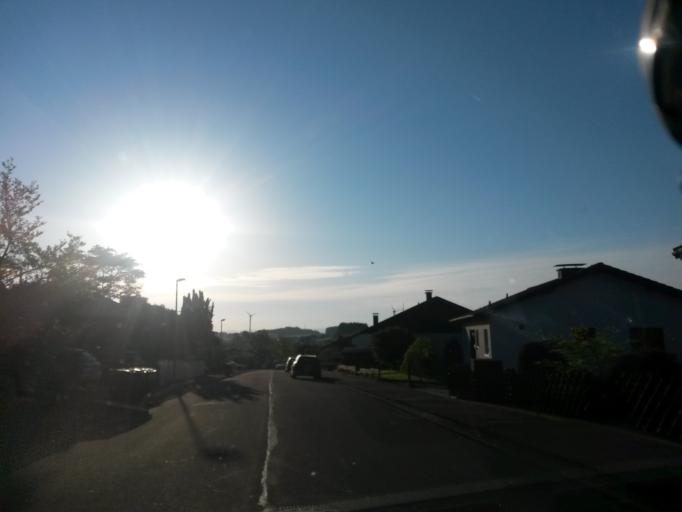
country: DE
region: North Rhine-Westphalia
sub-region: Regierungsbezirk Arnsberg
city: Herscheid
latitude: 51.1236
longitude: 7.7557
